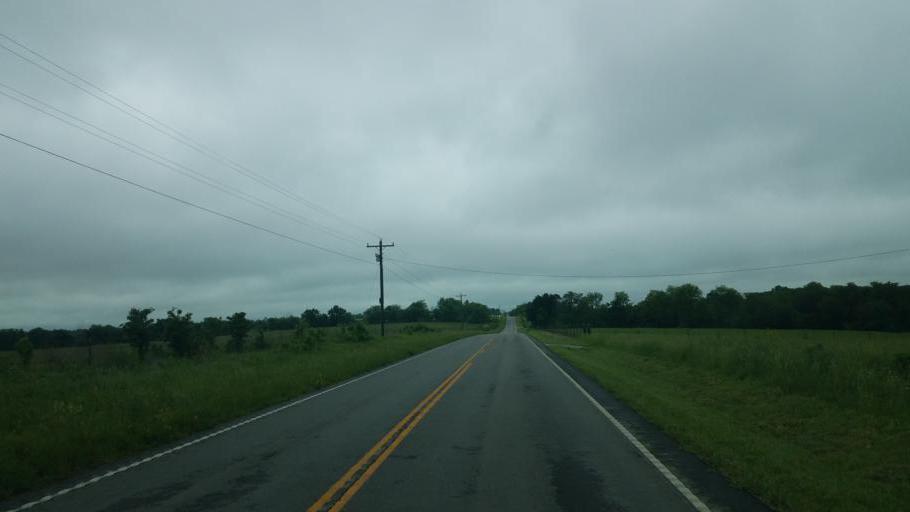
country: US
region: Missouri
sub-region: Moniteau County
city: California
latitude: 38.5070
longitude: -92.5701
